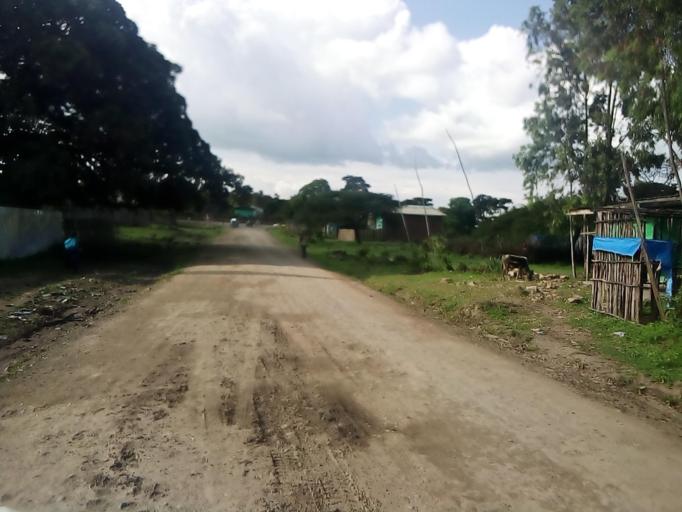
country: ET
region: Southern Nations, Nationalities, and People's Region
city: K'olito
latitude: 7.6648
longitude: 38.0469
